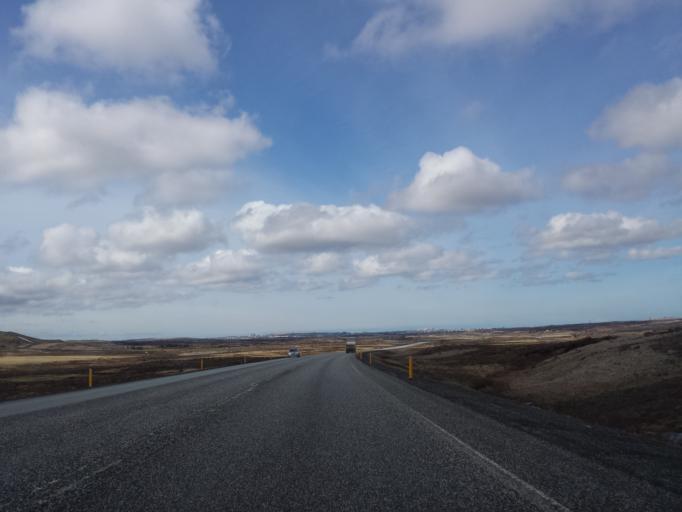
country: IS
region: Capital Region
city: Mosfellsbaer
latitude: 64.0723
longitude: -21.6309
